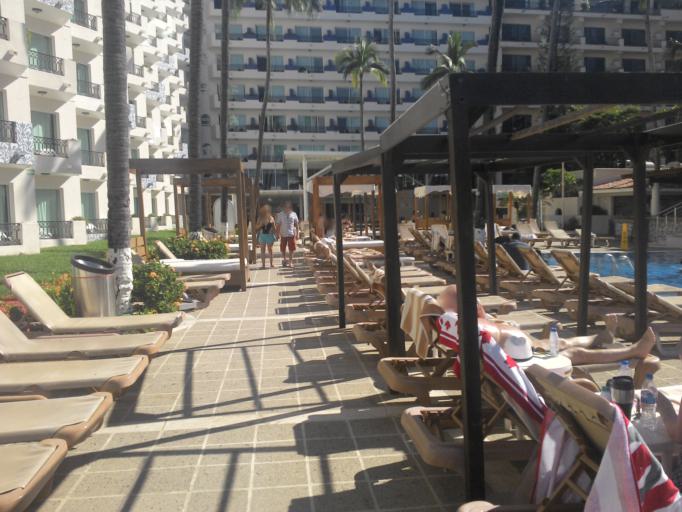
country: MX
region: Jalisco
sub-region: Puerto Vallarta
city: Puerto Vallarta
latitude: 20.6503
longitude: -105.2436
